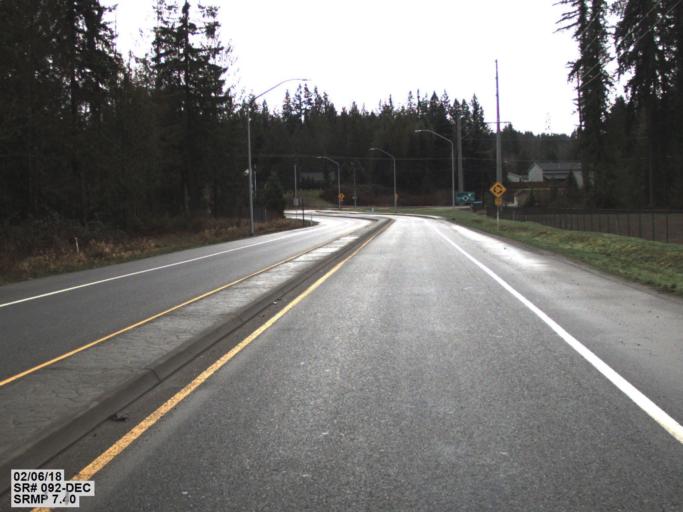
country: US
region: Washington
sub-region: Snohomish County
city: Granite Falls
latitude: 48.0851
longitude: -121.9907
